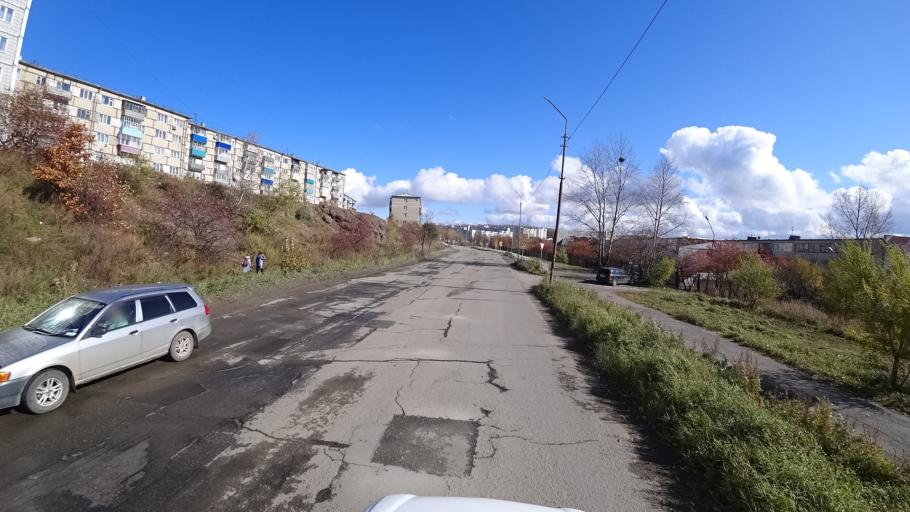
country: RU
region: Khabarovsk Krai
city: Amursk
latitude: 50.2423
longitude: 136.9076
